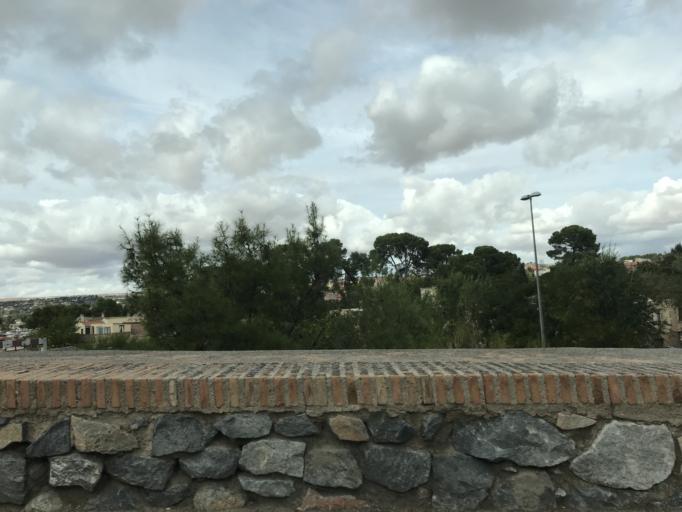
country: ES
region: Castille-La Mancha
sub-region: Province of Toledo
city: Toledo
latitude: 39.8621
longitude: -4.0283
